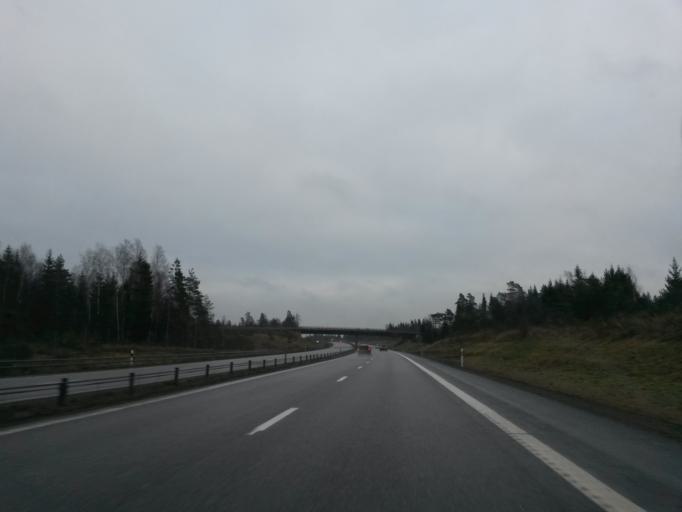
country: SE
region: Vaestra Goetaland
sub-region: Trollhattan
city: Sjuntorp
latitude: 58.3263
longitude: 12.1525
